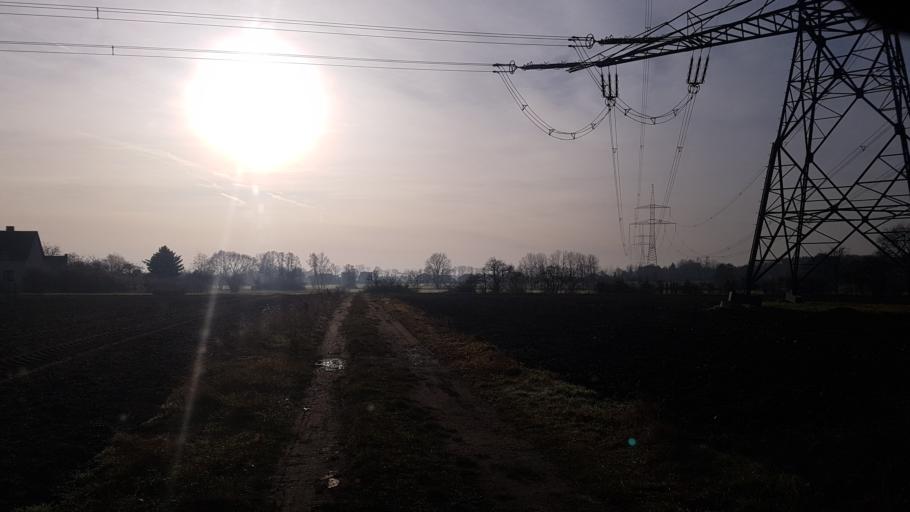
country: DE
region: Brandenburg
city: Doberlug-Kirchhain
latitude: 51.6419
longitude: 13.5422
